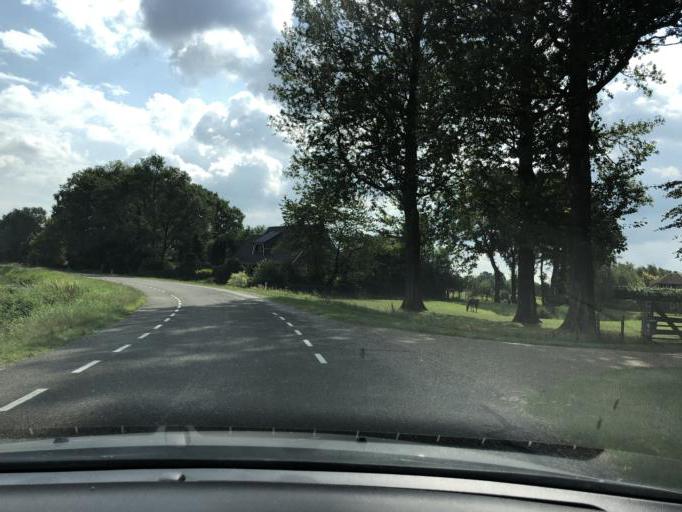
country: NL
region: Overijssel
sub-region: Gemeente Dalfsen
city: Dalfsen
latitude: 52.5779
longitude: 6.3546
